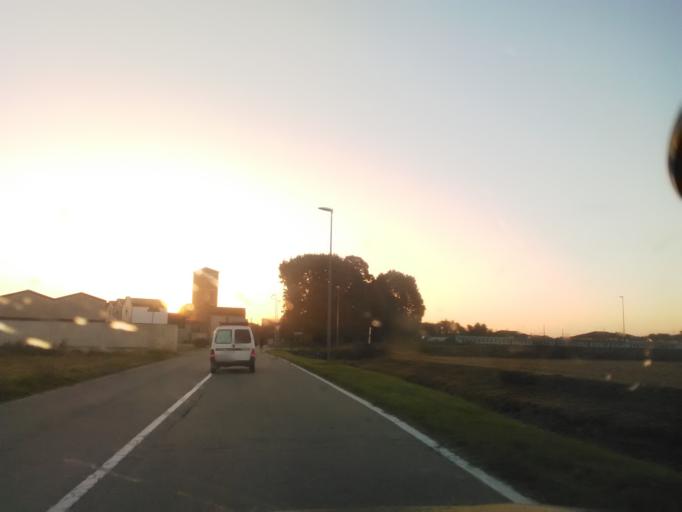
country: IT
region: Piedmont
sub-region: Provincia di Vercelli
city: Tronzano Vercellese
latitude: 45.3472
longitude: 8.1680
